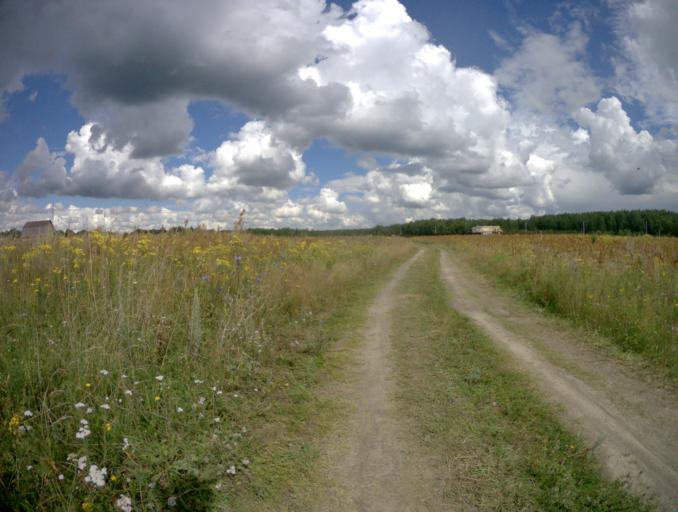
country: RU
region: Vladimir
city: Bogolyubovo
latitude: 56.1156
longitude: 40.5344
